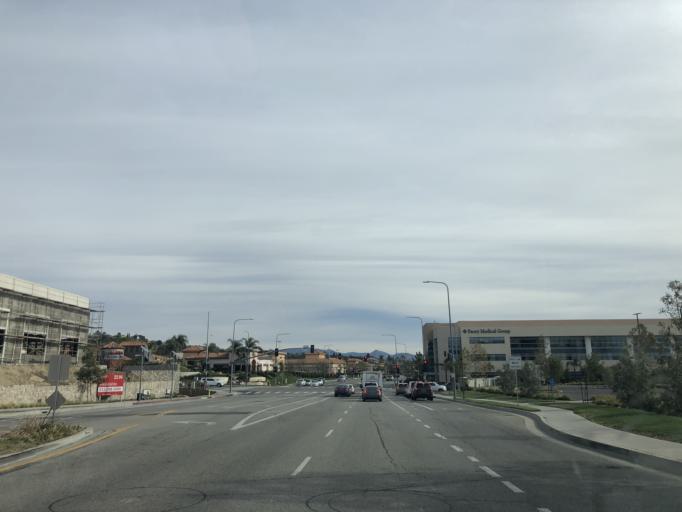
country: US
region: California
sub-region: Los Angeles County
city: Chatsworth
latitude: 34.2753
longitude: -118.5714
